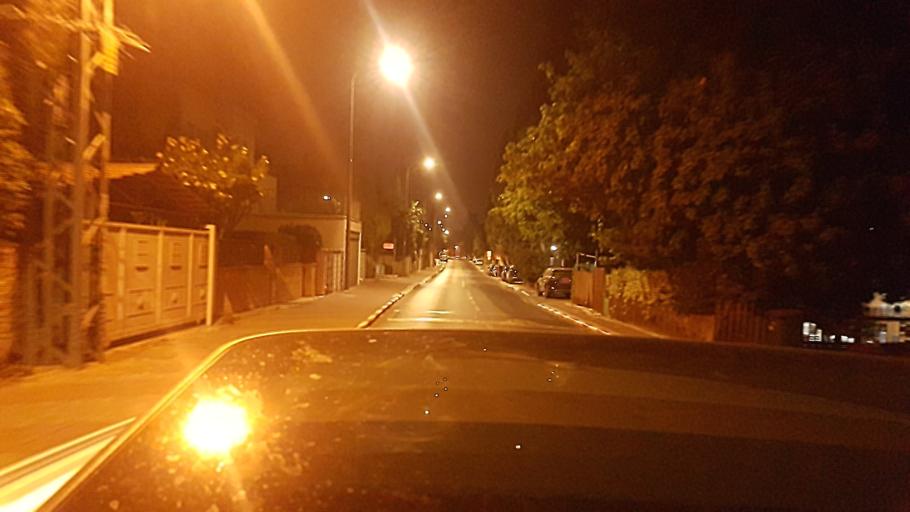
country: IL
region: Central District
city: Hod HaSharon
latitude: 32.1591
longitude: 34.8869
